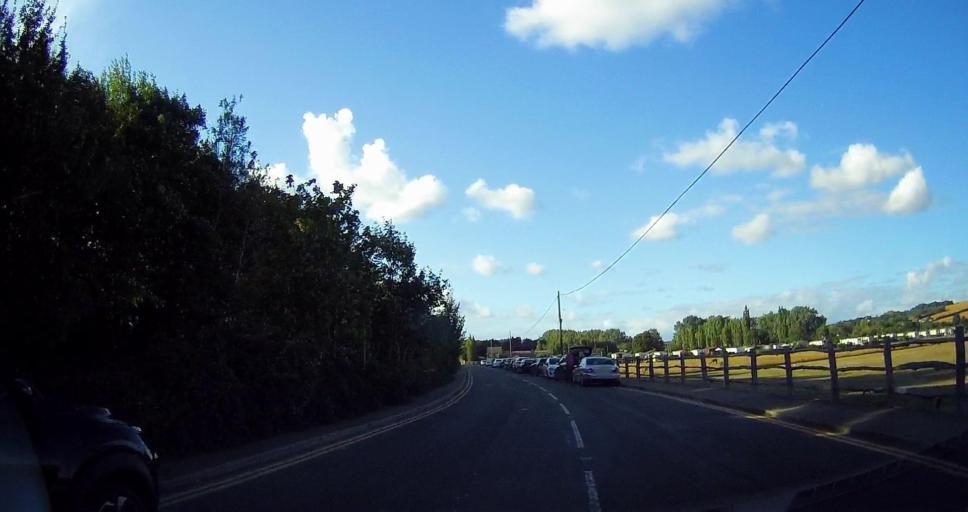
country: GB
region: England
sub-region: Kent
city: Yalding
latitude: 51.2240
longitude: 0.4185
